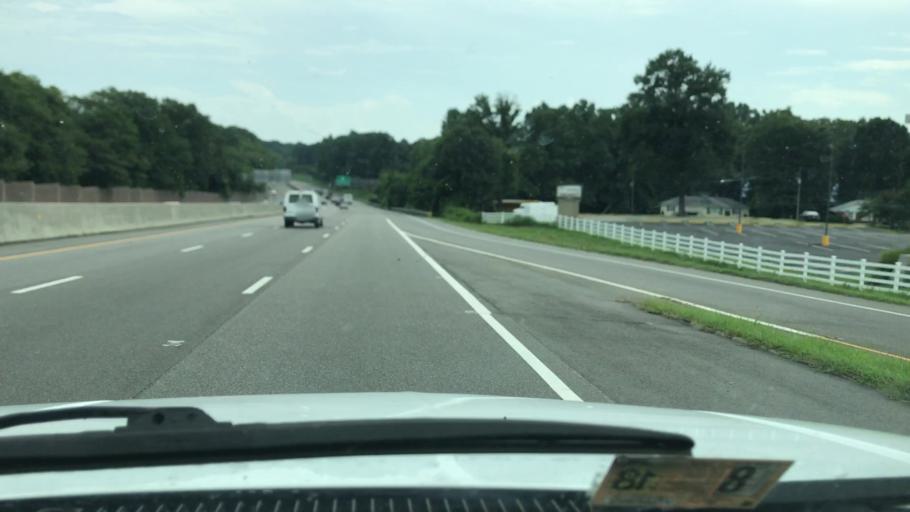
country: US
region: Virginia
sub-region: Chesterfield County
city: Bon Air
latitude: 37.4769
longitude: -77.5146
